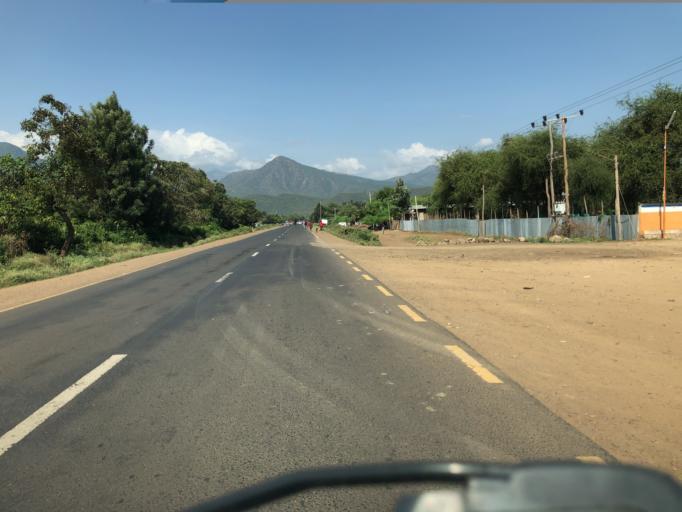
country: ET
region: Southern Nations, Nationalities, and People's Region
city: Arba Minch'
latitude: 6.2880
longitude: 37.7743
